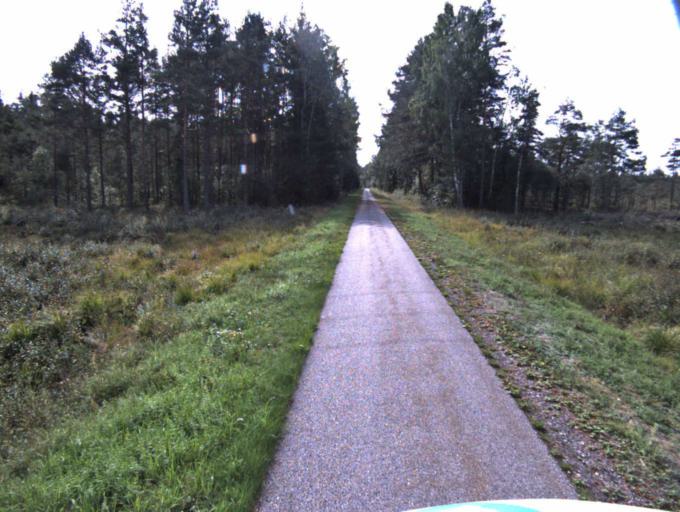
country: SE
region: Vaestra Goetaland
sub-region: Tranemo Kommun
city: Limmared
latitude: 57.6169
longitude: 13.3440
